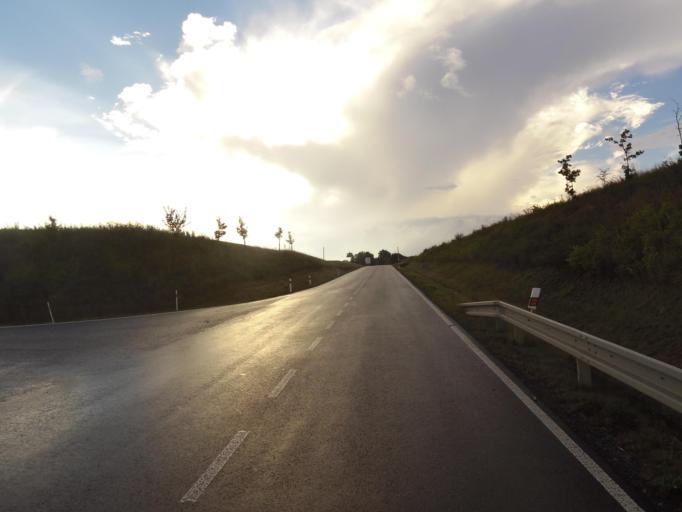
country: CZ
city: Duba
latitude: 50.5419
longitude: 14.5291
